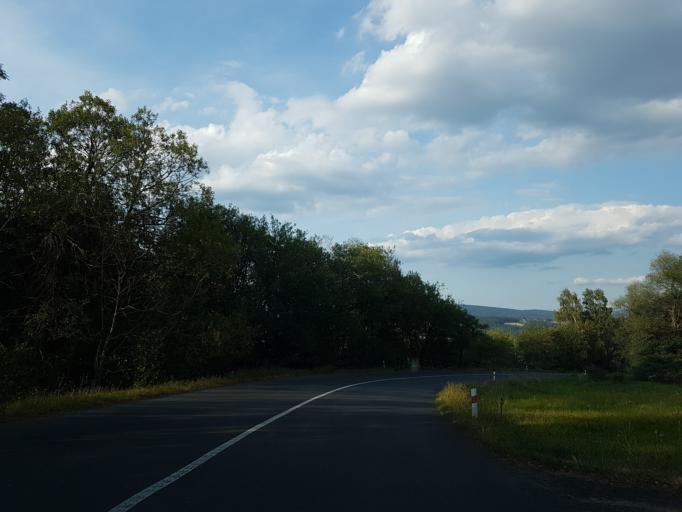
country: CZ
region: Liberecky
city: Mala Skala
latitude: 50.6643
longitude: 15.1684
